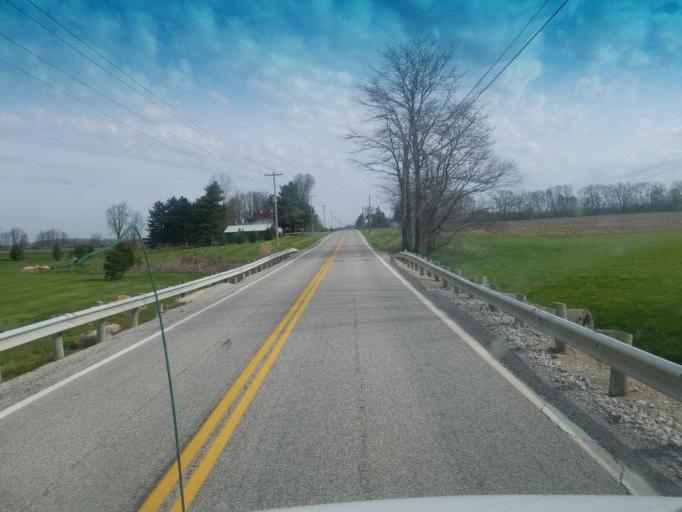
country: US
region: Ohio
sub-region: Marion County
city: Prospect
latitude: 40.4213
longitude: -83.1973
